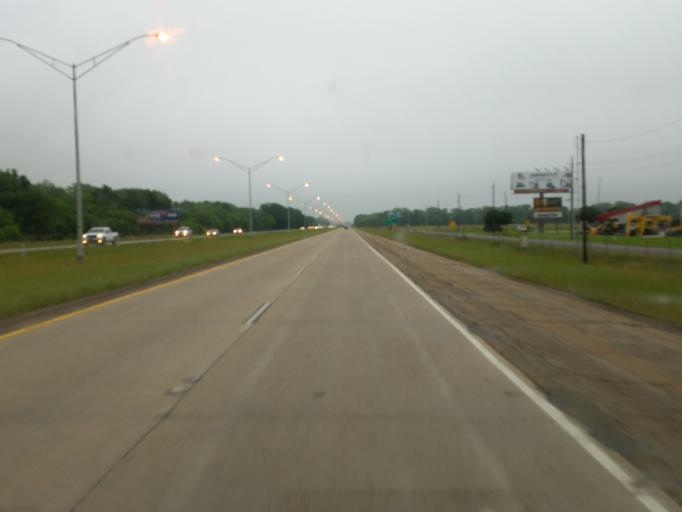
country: US
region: Louisiana
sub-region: Bossier Parish
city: Red Chute
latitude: 32.5333
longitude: -93.6551
